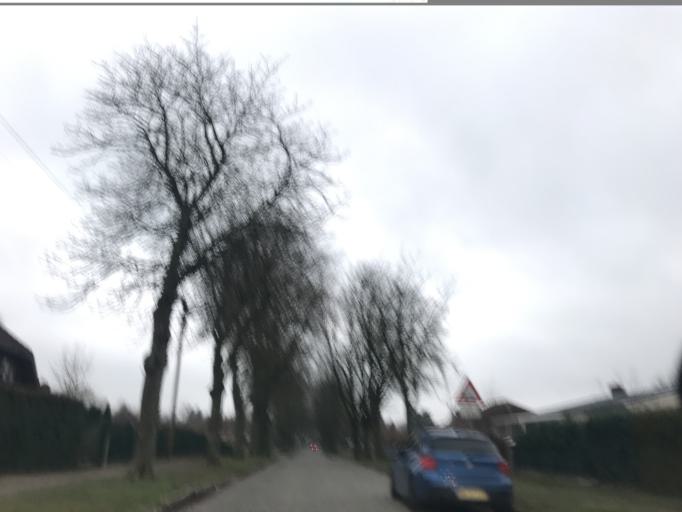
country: DE
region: Brandenburg
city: Falkensee
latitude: 52.5606
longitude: 13.1133
